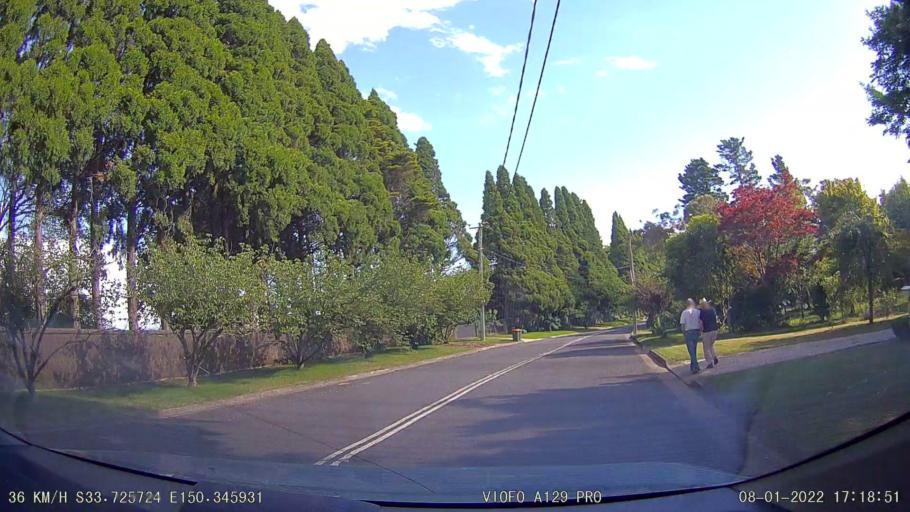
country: AU
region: New South Wales
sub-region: Blue Mountains Municipality
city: Leura
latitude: -33.7257
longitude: 150.3459
